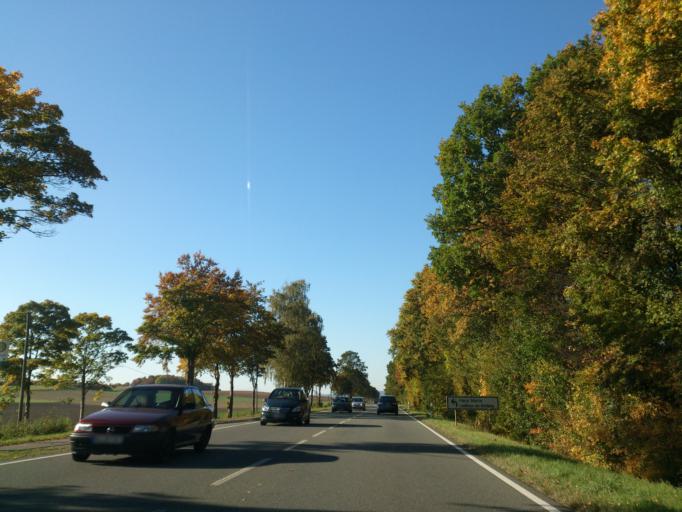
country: DE
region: North Rhine-Westphalia
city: Warburg
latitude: 51.5019
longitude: 9.1080
